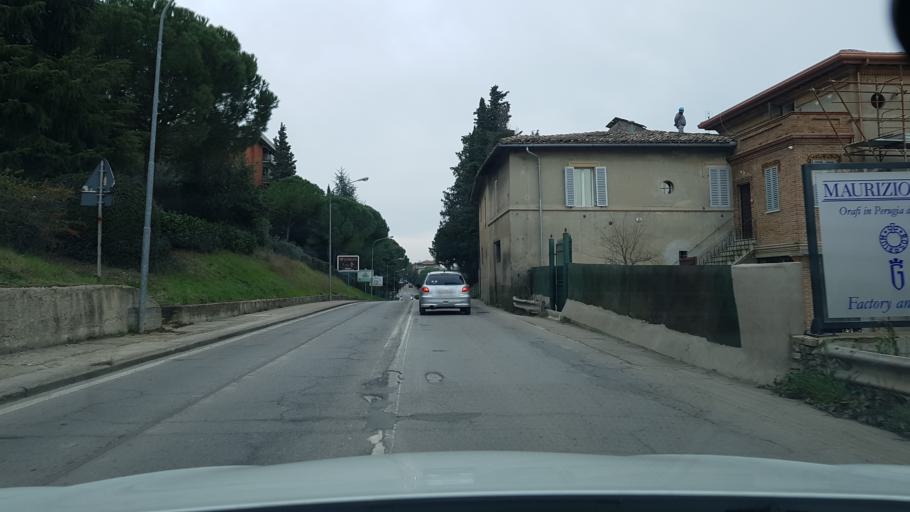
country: IT
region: Umbria
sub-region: Provincia di Perugia
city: Lacugnano
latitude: 43.1041
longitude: 12.3427
